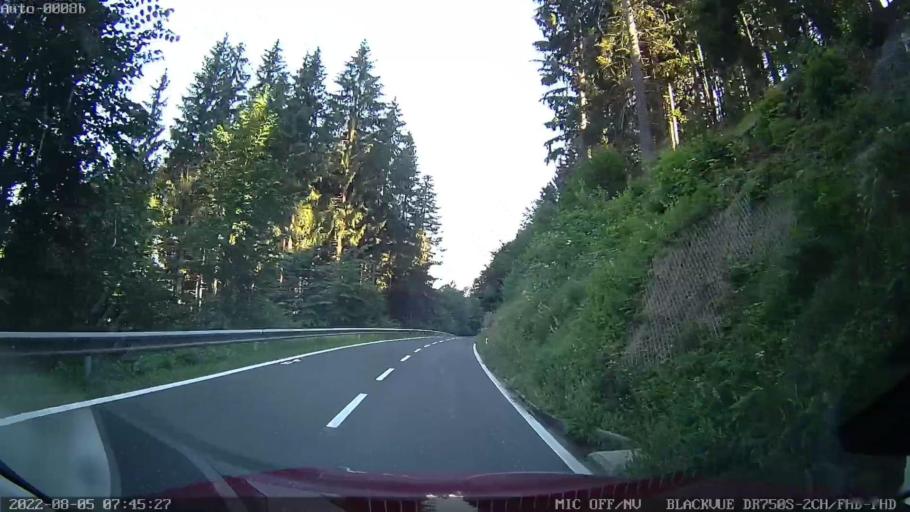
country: AT
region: Carinthia
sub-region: Politischer Bezirk Villach Land
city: Arnoldstein
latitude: 46.5327
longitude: 13.7485
